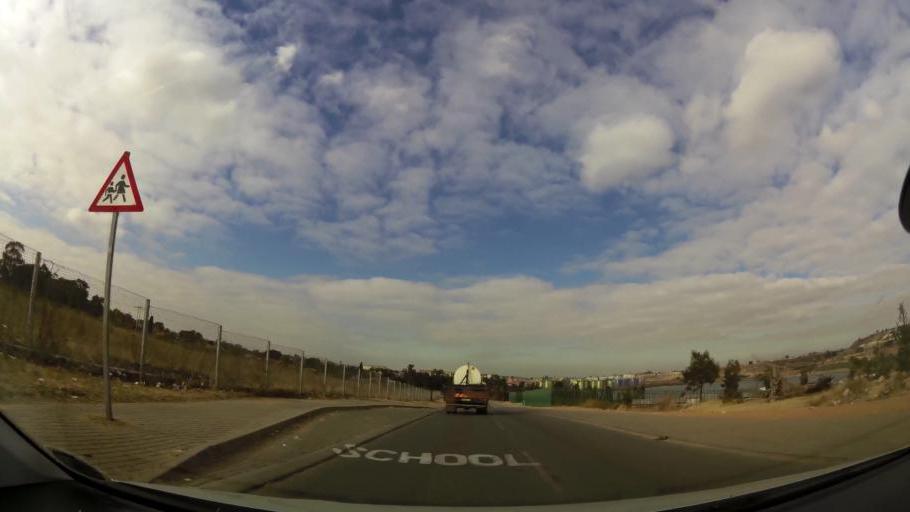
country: ZA
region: Gauteng
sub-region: City of Johannesburg Metropolitan Municipality
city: Roodepoort
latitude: -26.1958
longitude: 27.9106
